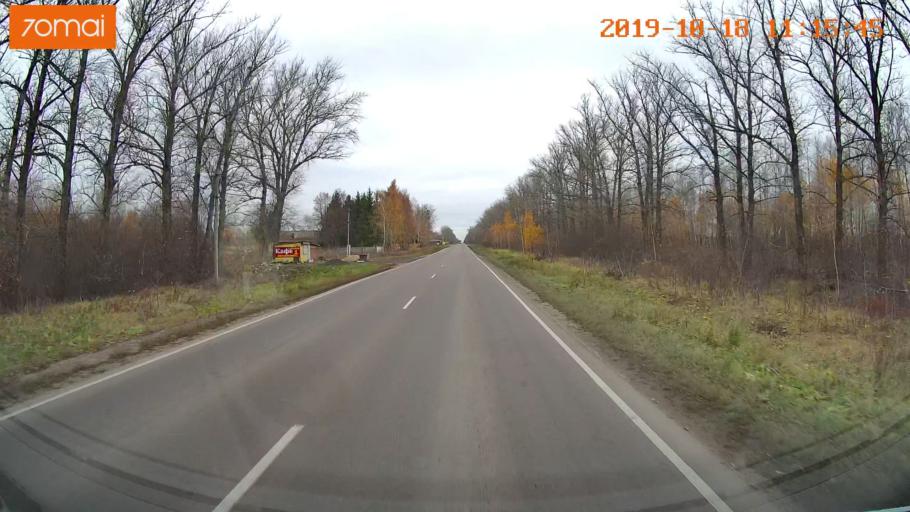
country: RU
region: Tula
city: Kimovsk
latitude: 53.9967
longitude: 38.5478
